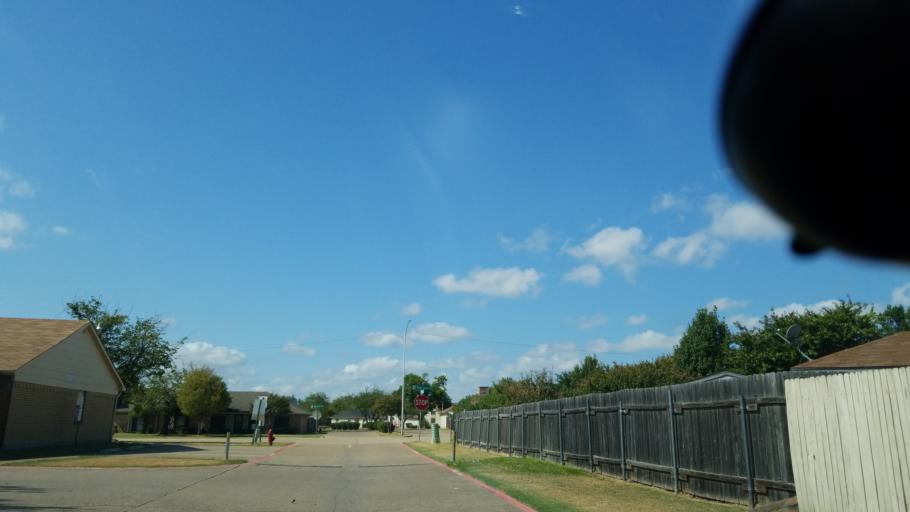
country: US
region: Texas
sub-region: Dallas County
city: Grand Prairie
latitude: 32.6972
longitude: -96.9885
